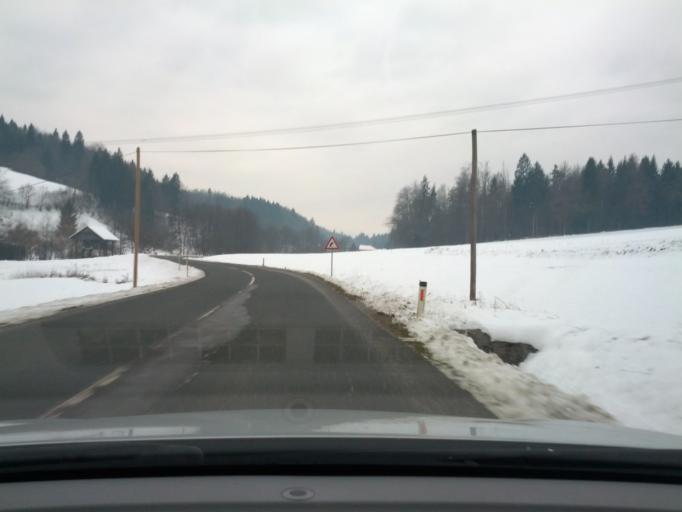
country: SI
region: Litija
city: Litija
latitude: 46.1347
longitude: 14.8230
